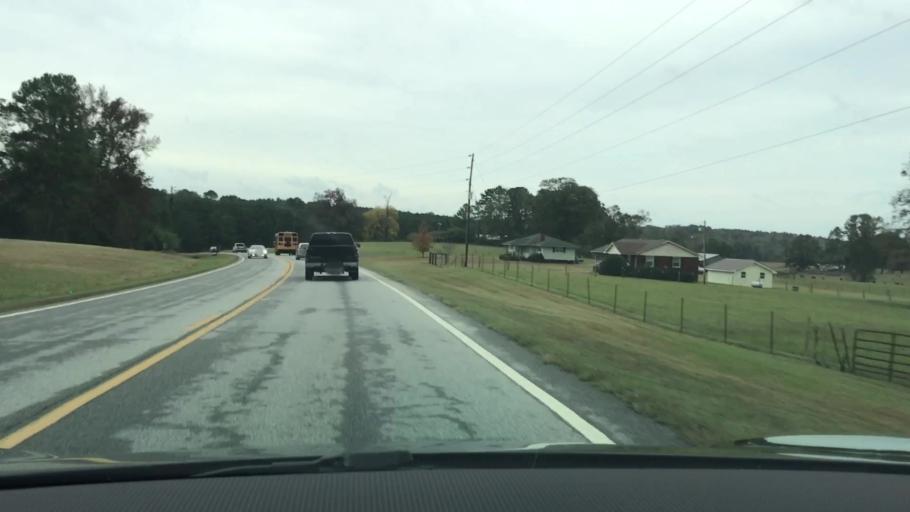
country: US
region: Georgia
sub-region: Greene County
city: Greensboro
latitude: 33.6466
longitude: -83.2333
